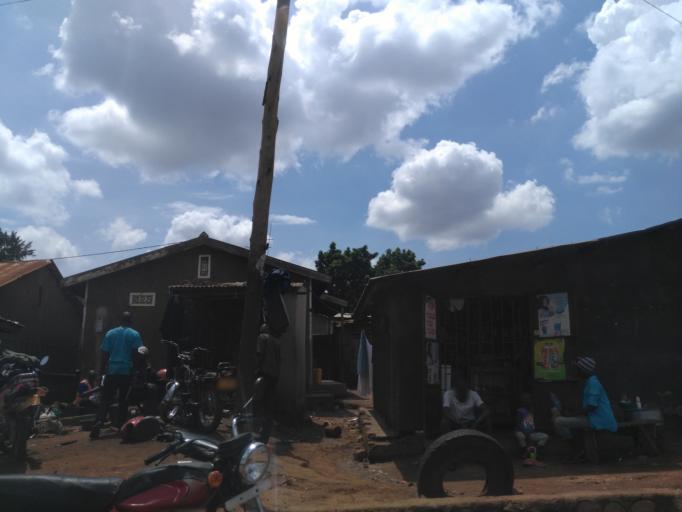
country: UG
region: Central Region
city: Kampala Central Division
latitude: 0.3475
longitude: 32.5778
